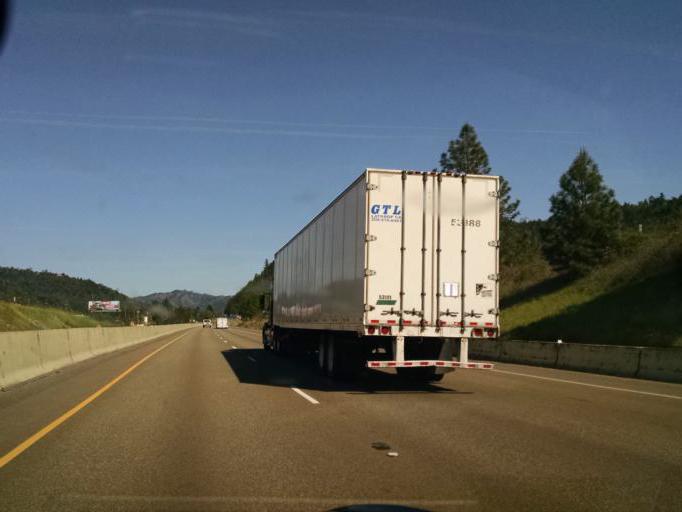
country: US
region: Oregon
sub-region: Douglas County
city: Tri-City
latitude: 42.9480
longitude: -123.3136
